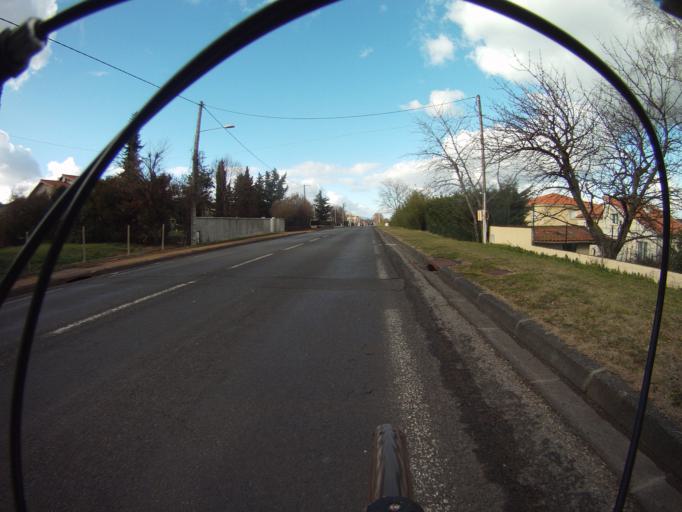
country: FR
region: Auvergne
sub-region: Departement du Puy-de-Dome
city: Perignat-les-Sarlieve
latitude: 45.7287
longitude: 3.1451
